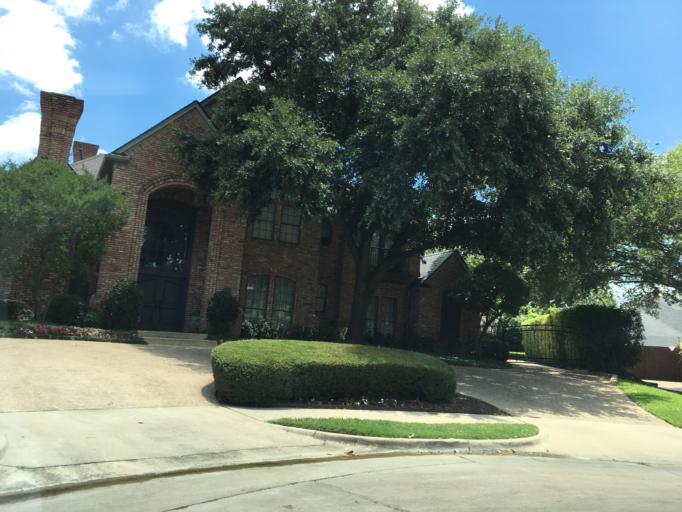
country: US
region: Texas
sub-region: Dallas County
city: Farmers Branch
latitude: 32.9257
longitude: -96.8576
